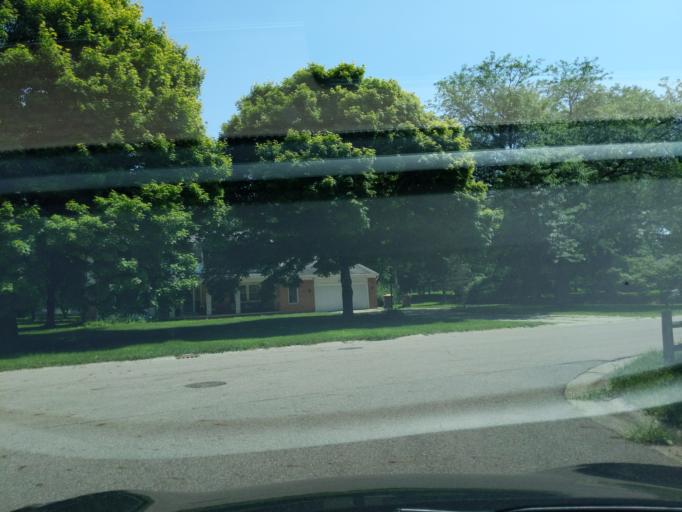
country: US
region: Michigan
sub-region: Eaton County
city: Waverly
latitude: 42.7660
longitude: -84.6137
